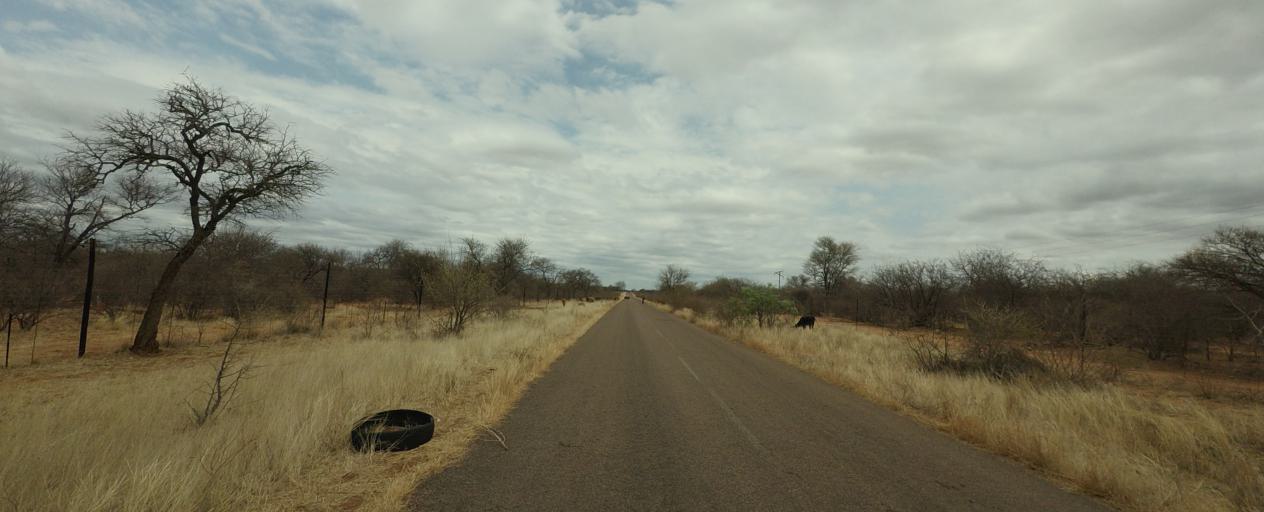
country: BW
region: Central
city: Mathathane
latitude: -22.6626
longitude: 28.7037
